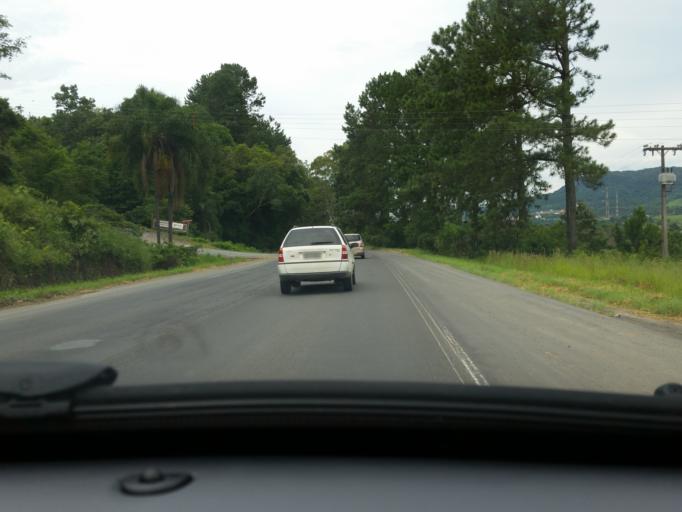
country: BR
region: Santa Catarina
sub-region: Rio Do Sul
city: Rio do Sul
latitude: -27.2545
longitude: -49.7056
